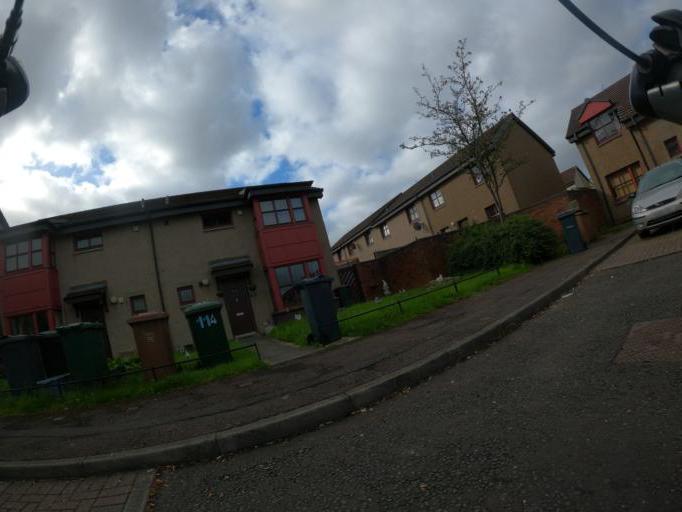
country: GB
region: Scotland
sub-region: Edinburgh
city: Colinton
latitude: 55.9690
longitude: -3.2586
